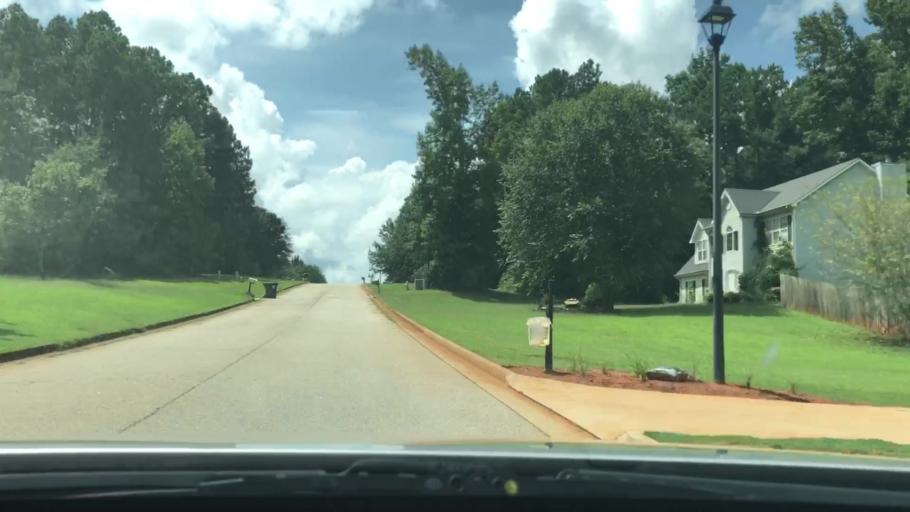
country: US
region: Georgia
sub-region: Henry County
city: McDonough
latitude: 33.4110
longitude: -84.1136
